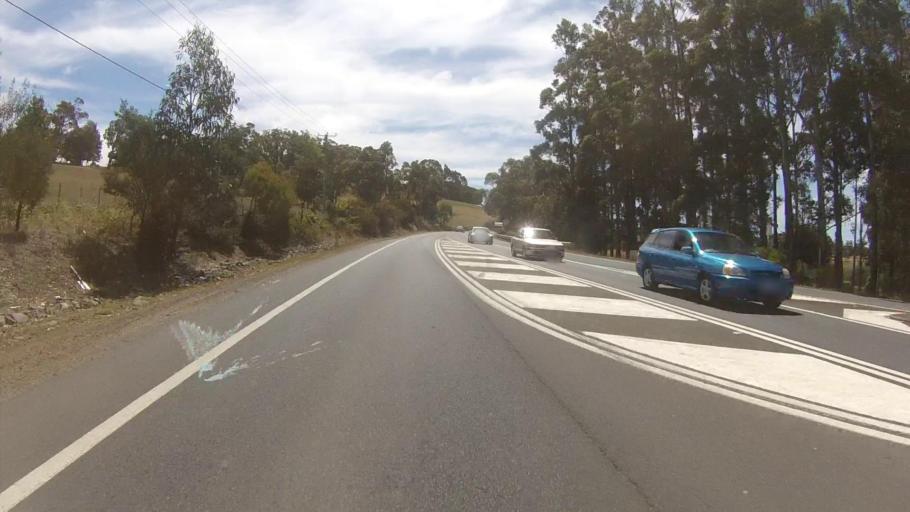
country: AU
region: Tasmania
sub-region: Kingborough
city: Margate
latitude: -43.0072
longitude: 147.2724
